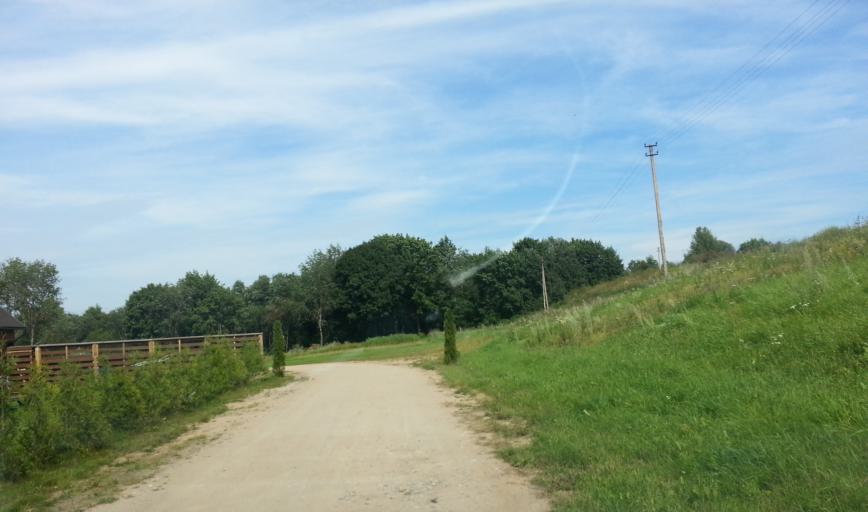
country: LT
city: Grigiskes
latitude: 54.7361
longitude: 25.0730
